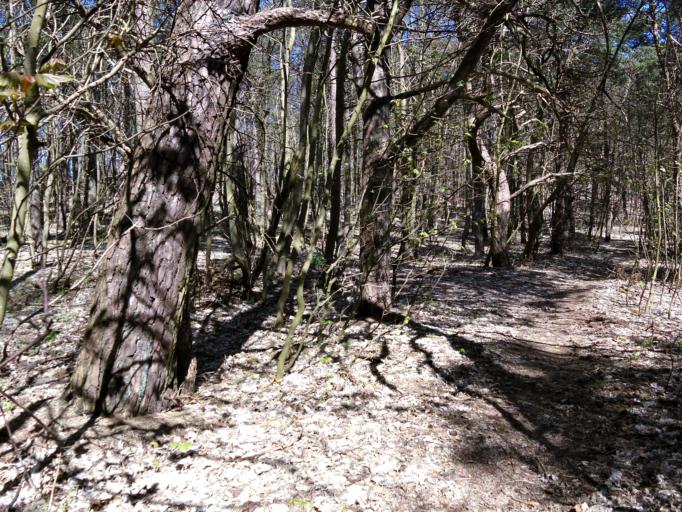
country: DE
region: Mecklenburg-Vorpommern
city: Hiddensee
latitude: 54.5941
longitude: 13.1108
